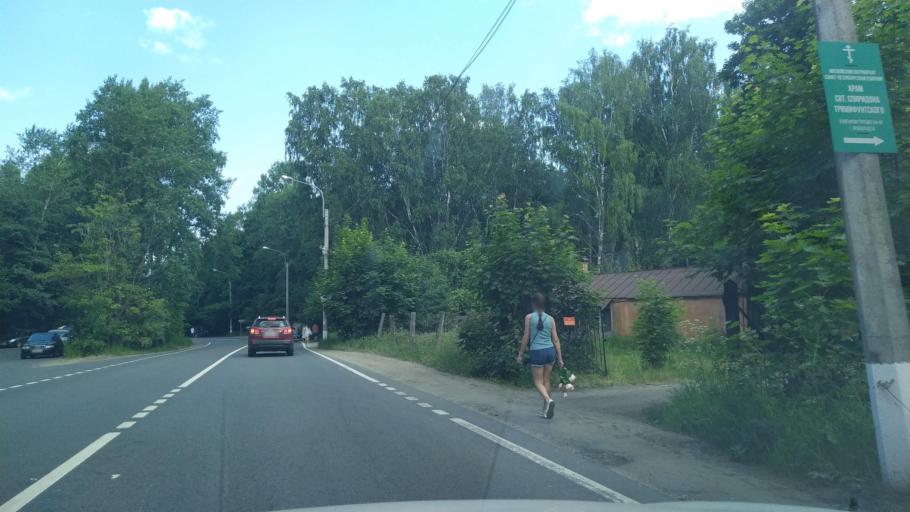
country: RU
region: St.-Petersburg
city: Kronshtadt
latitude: 60.0155
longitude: 29.7136
